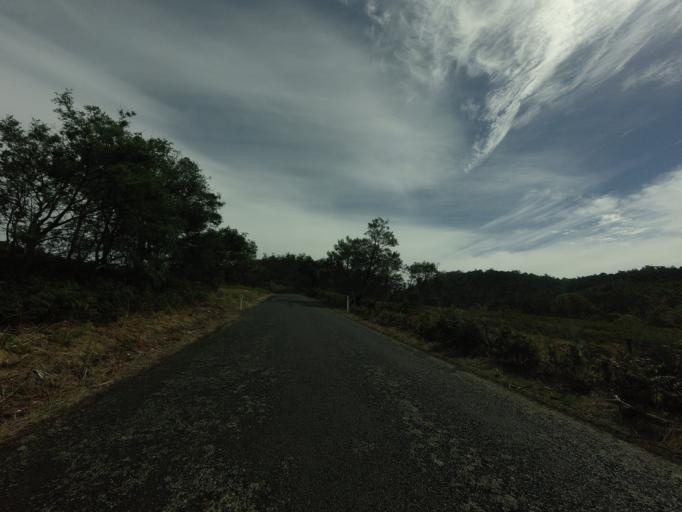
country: AU
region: Tasmania
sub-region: Sorell
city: Sorell
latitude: -42.5715
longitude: 147.6933
